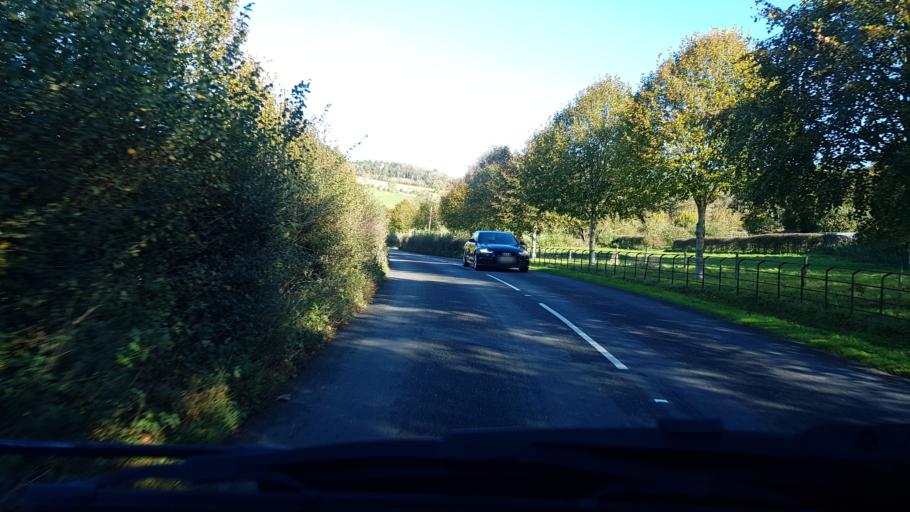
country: GB
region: England
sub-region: Surrey
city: Chilworth
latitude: 51.2225
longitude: -0.4846
